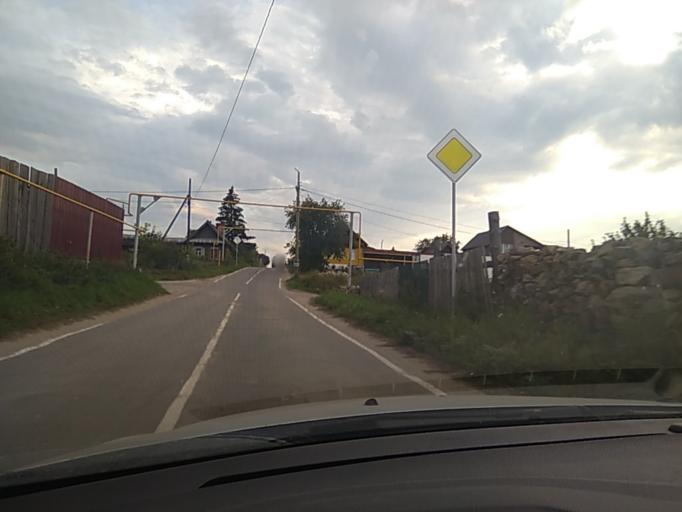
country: RU
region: Chelyabinsk
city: Kyshtym
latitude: 55.6994
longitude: 60.5310
